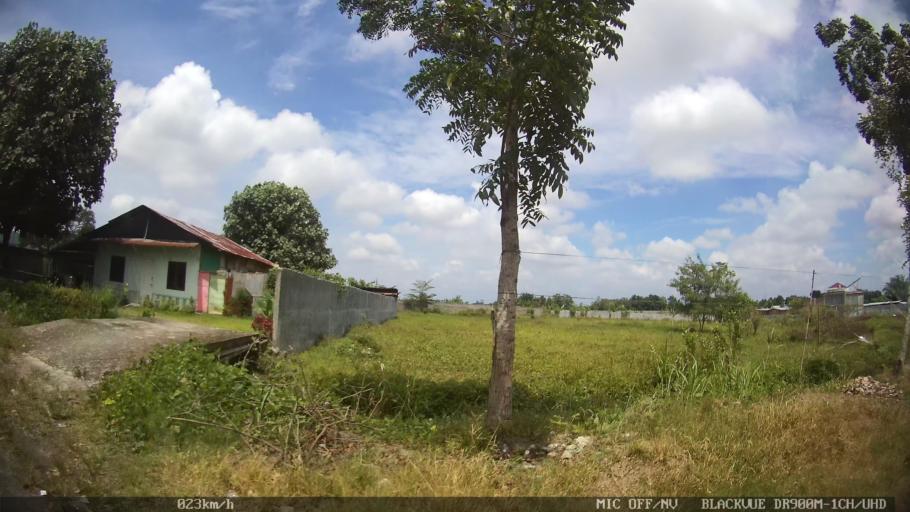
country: ID
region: North Sumatra
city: Percut
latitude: 3.6174
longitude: 98.7815
